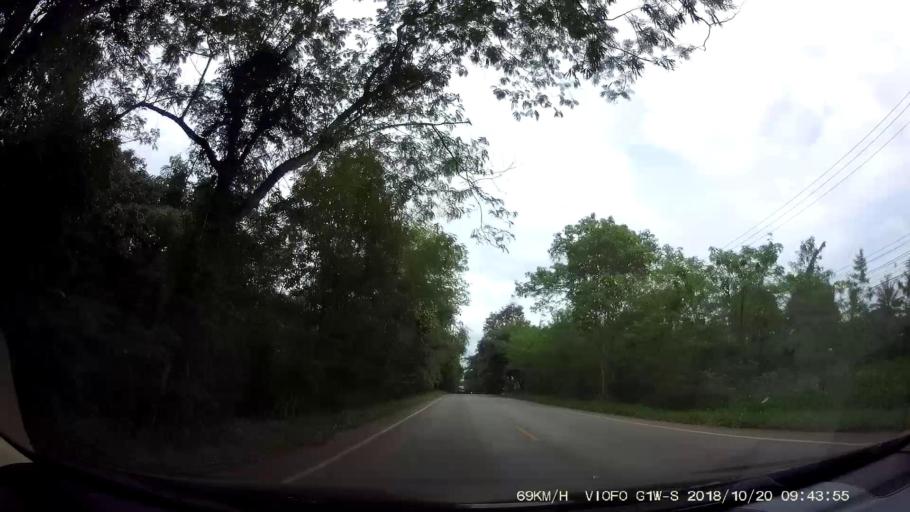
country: TH
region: Chaiyaphum
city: Khon San
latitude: 16.4781
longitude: 101.9461
